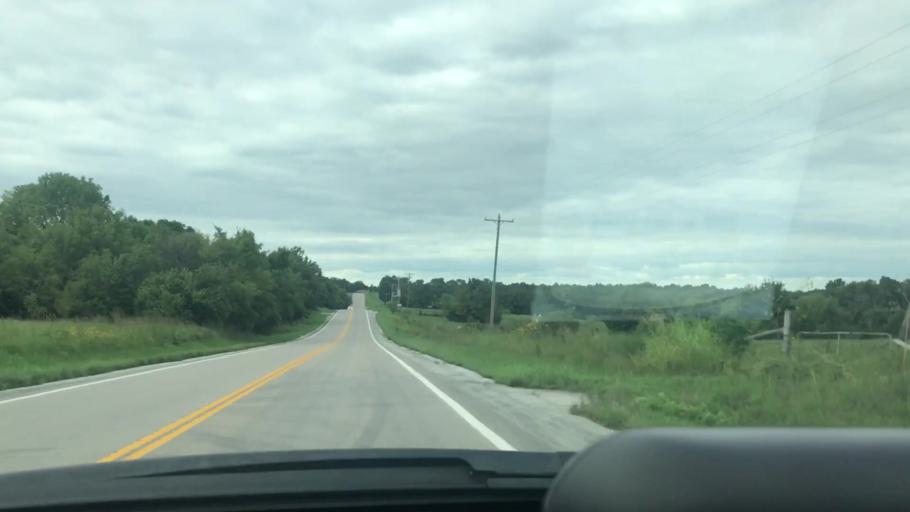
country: US
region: Missouri
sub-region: Benton County
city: Warsaw
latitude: 38.1466
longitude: -93.2913
